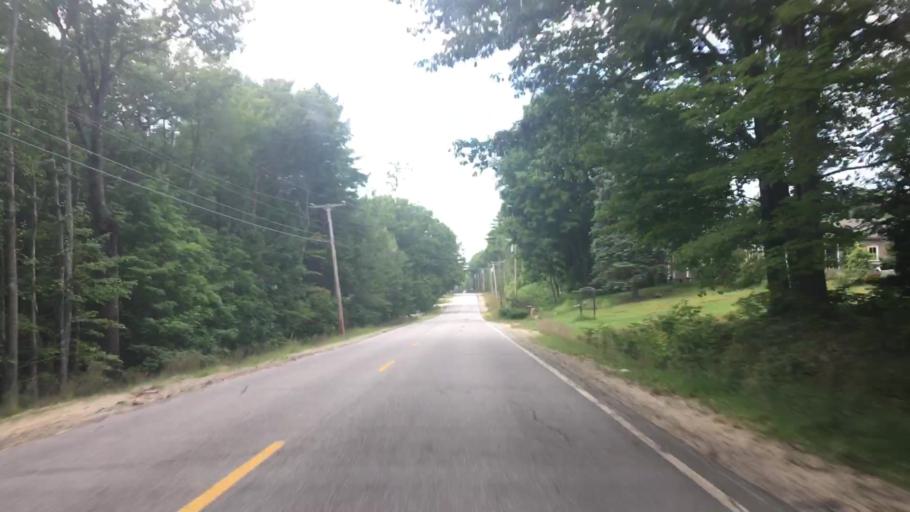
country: US
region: Maine
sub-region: Oxford County
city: Oxford
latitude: 44.0494
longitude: -70.5487
